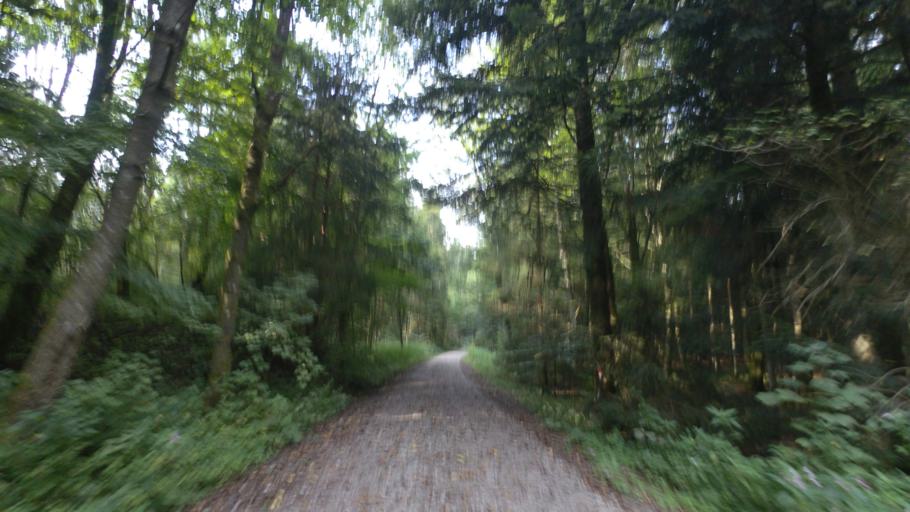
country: DE
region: Bavaria
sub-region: Upper Bavaria
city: Chieming
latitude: 47.9248
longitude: 12.5604
